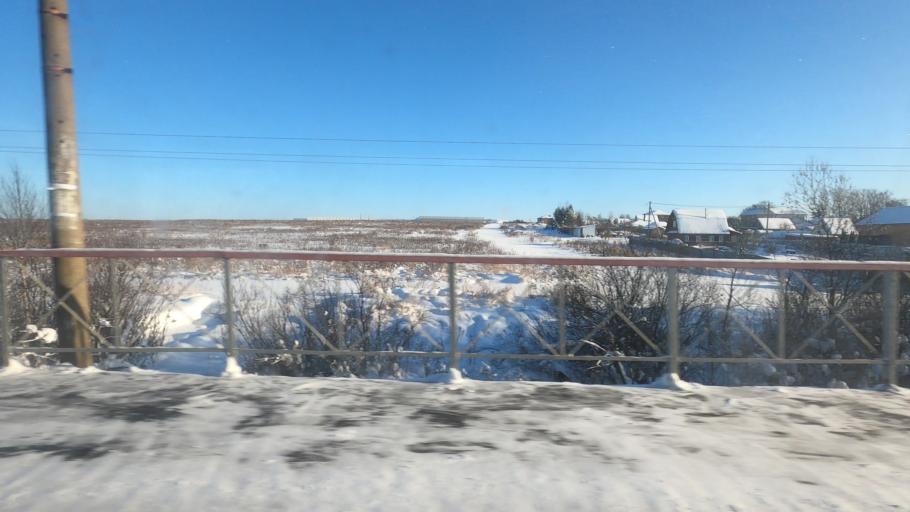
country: RU
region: Moskovskaya
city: Orud'yevo
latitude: 56.4182
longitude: 37.4973
